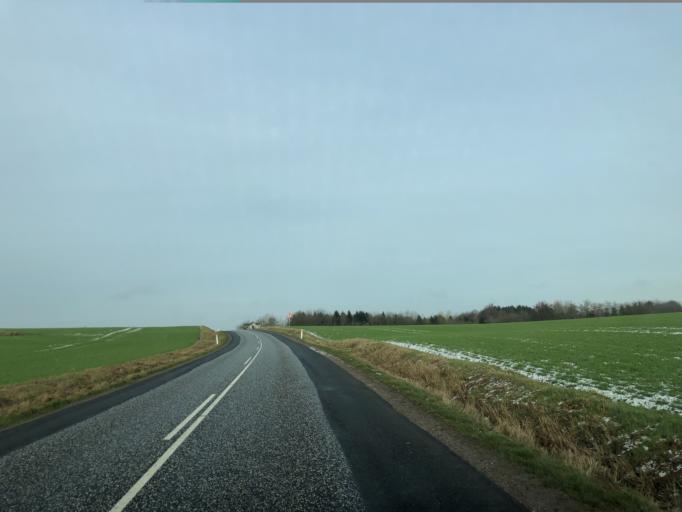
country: DK
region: Central Jutland
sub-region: Hedensted Kommune
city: Torring
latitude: 55.8178
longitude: 9.4740
